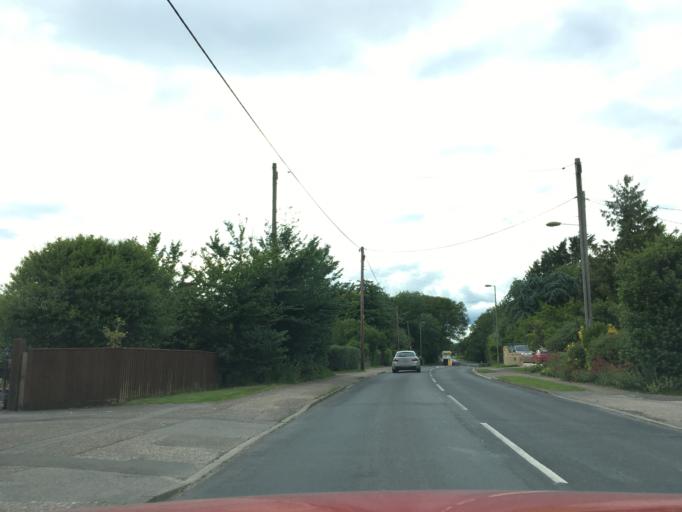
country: GB
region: England
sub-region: Oxfordshire
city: Boars Hill
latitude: 51.7081
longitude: -1.3213
